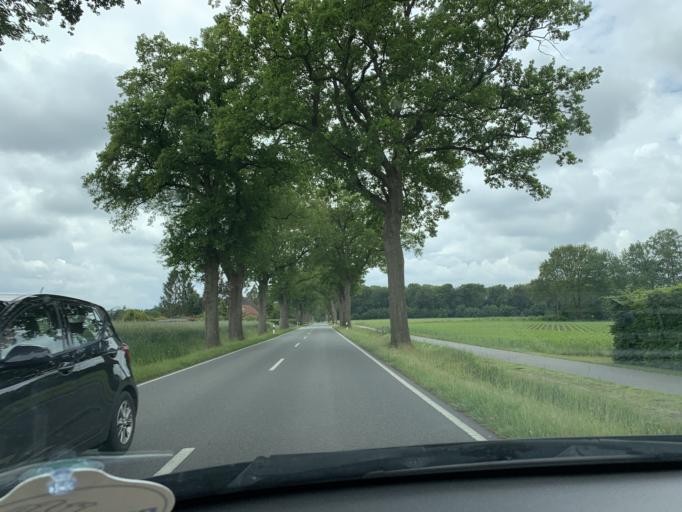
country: DE
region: Lower Saxony
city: Westerstede
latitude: 53.2885
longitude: 7.9864
